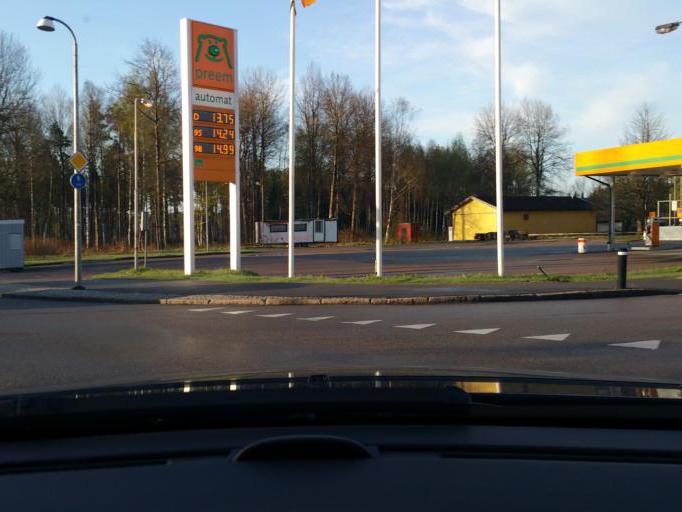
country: SE
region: Kronoberg
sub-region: Vaxjo Kommun
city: Lammhult
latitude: 57.1696
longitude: 14.5799
